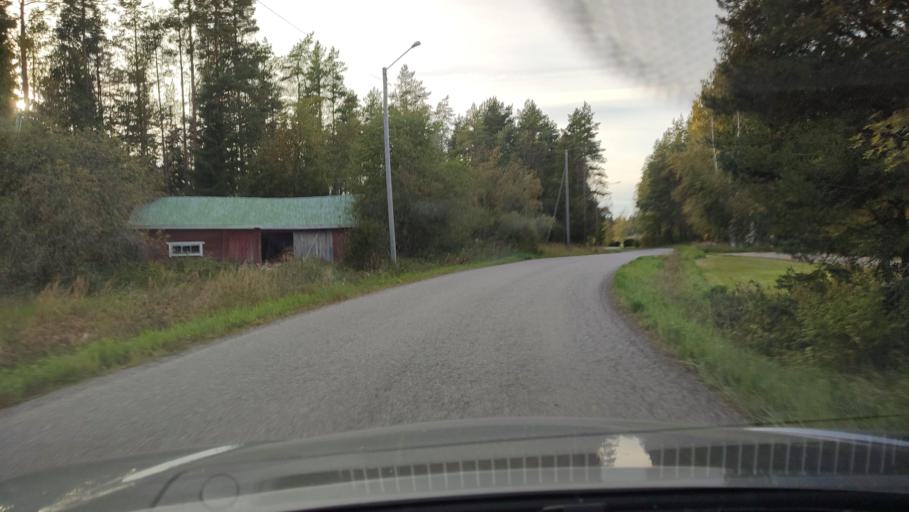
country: FI
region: Southern Ostrobothnia
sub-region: Suupohja
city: Karijoki
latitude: 62.1278
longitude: 21.5844
